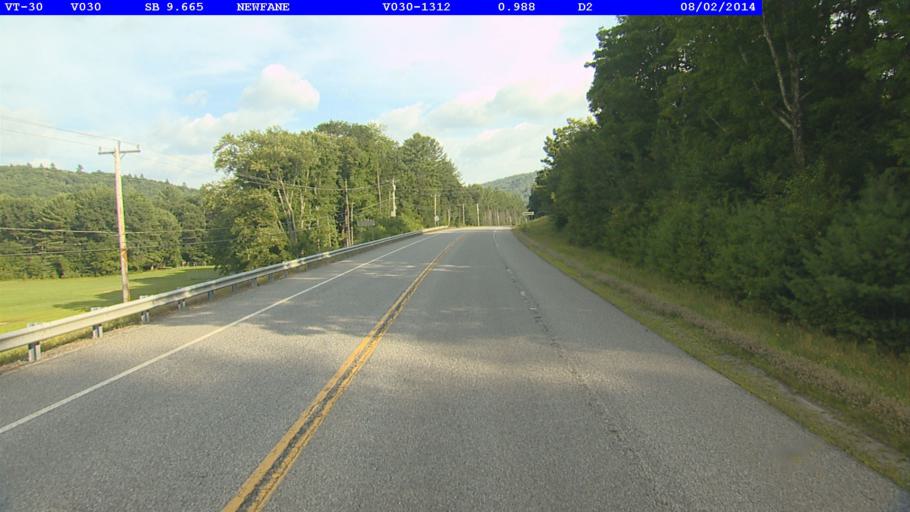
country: US
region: Vermont
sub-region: Windham County
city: Newfane
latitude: 42.9595
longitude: -72.6512
